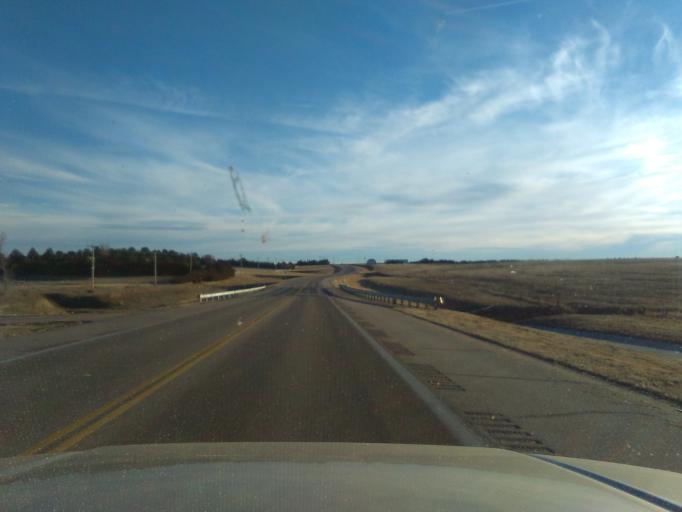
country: US
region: Kansas
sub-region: Logan County
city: Oakley
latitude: 39.1846
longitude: -100.8699
